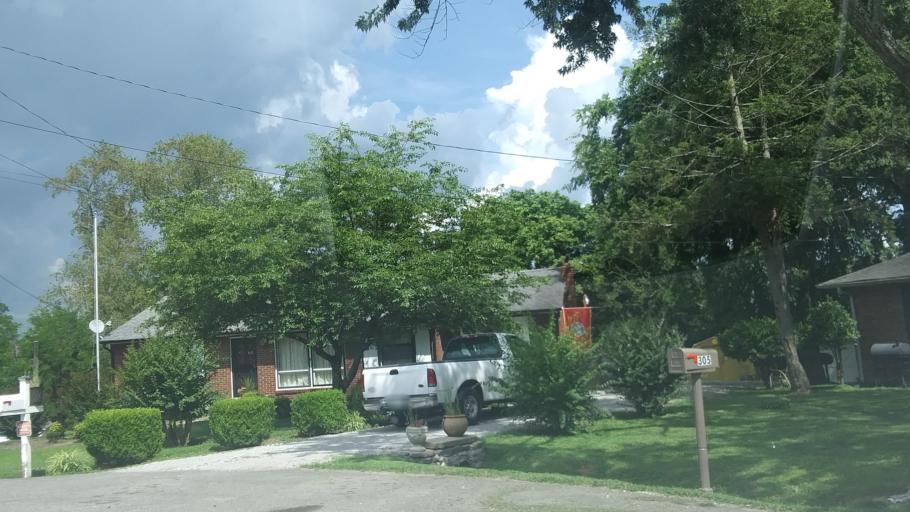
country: US
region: Tennessee
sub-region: Davidson County
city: Oak Hill
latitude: 36.0730
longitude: -86.7035
